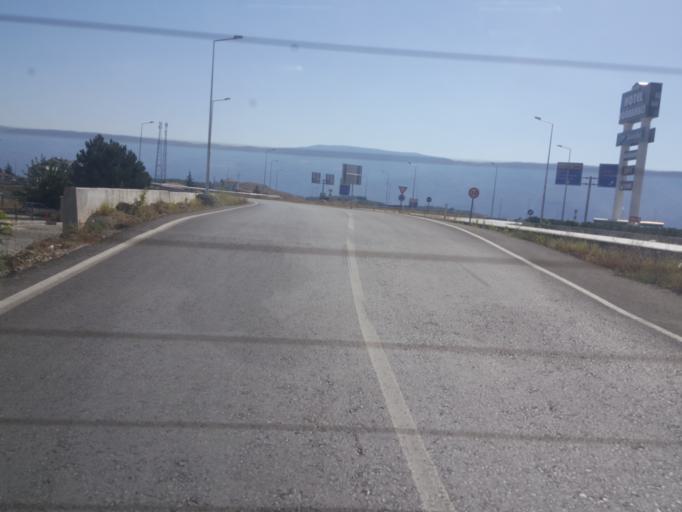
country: TR
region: Kastamonu
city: Tosya
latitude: 41.0079
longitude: 34.0570
